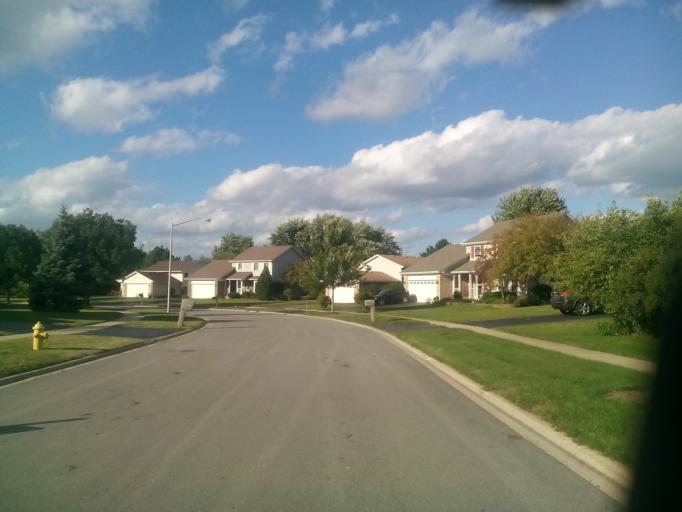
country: US
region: Illinois
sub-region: Will County
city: Bolingbrook
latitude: 41.7005
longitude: -88.1444
